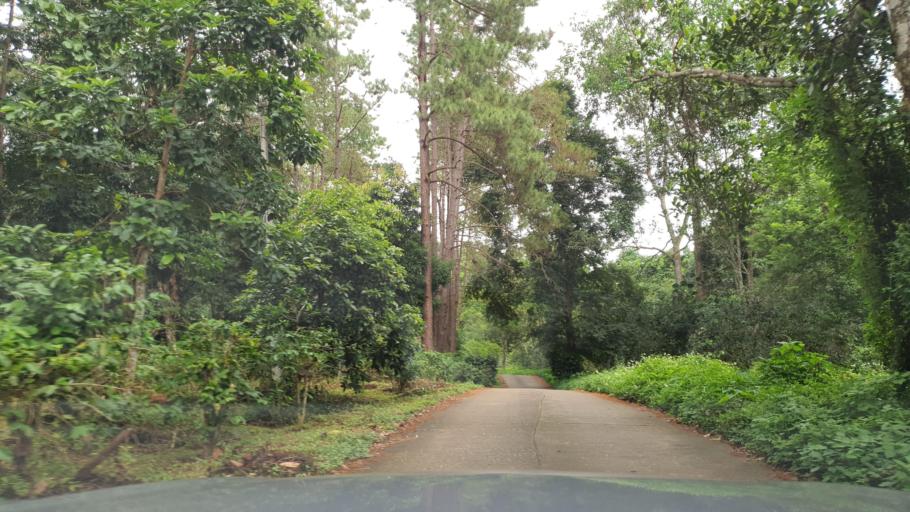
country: TH
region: Chiang Mai
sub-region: Amphoe Chiang Dao
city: Chiang Dao
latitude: 19.2529
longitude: 98.9219
